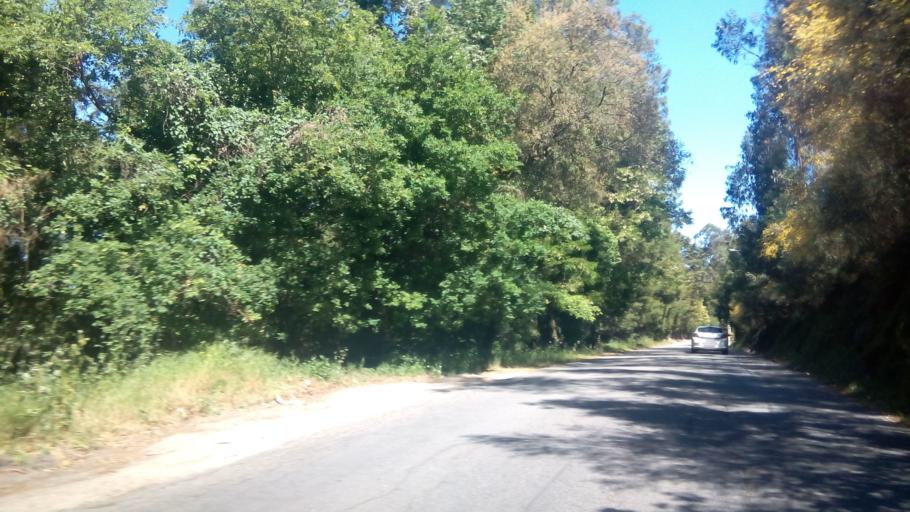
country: PT
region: Porto
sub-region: Paredes
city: Baltar
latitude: 41.1832
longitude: -8.3579
